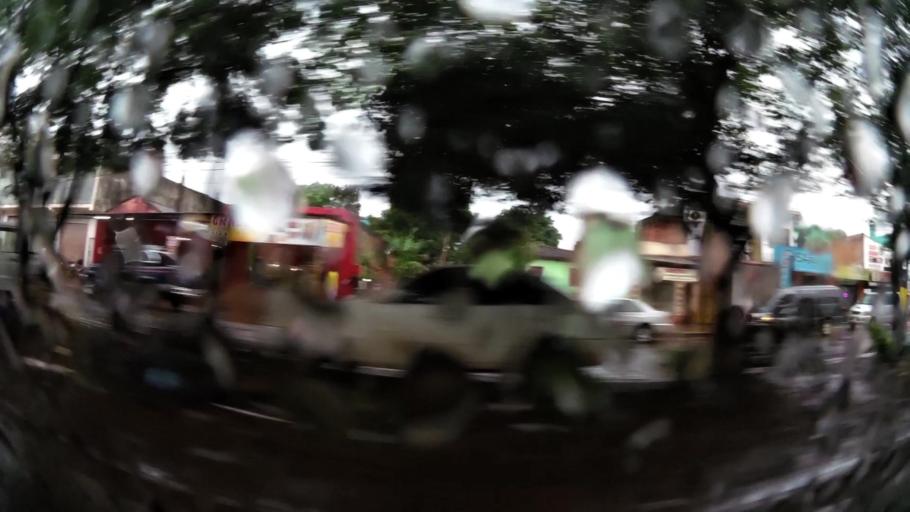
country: PY
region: Alto Parana
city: Presidente Franco
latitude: -25.5112
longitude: -54.6717
